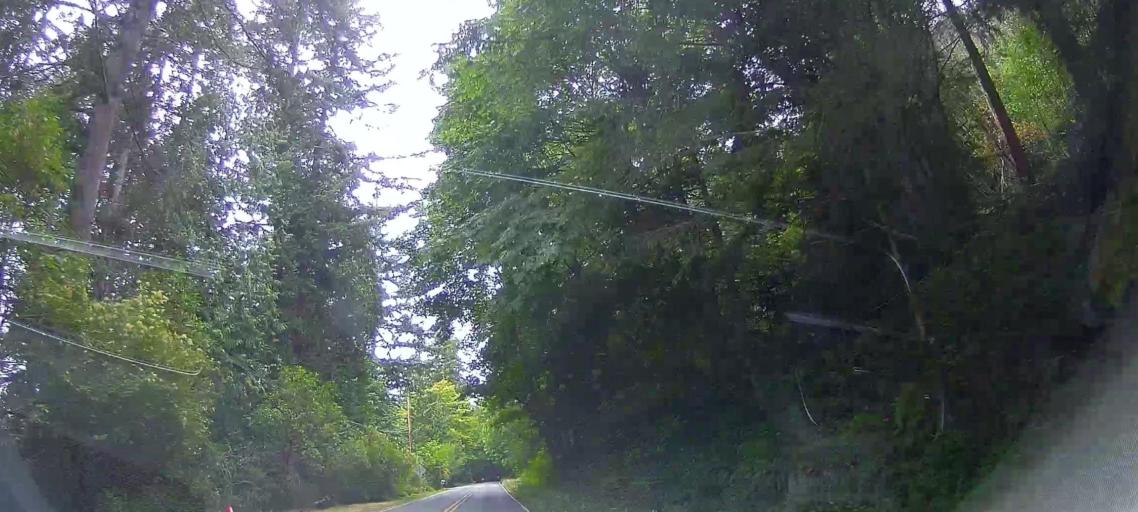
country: US
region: Washington
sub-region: Skagit County
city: Anacortes
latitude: 48.4529
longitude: -122.6336
